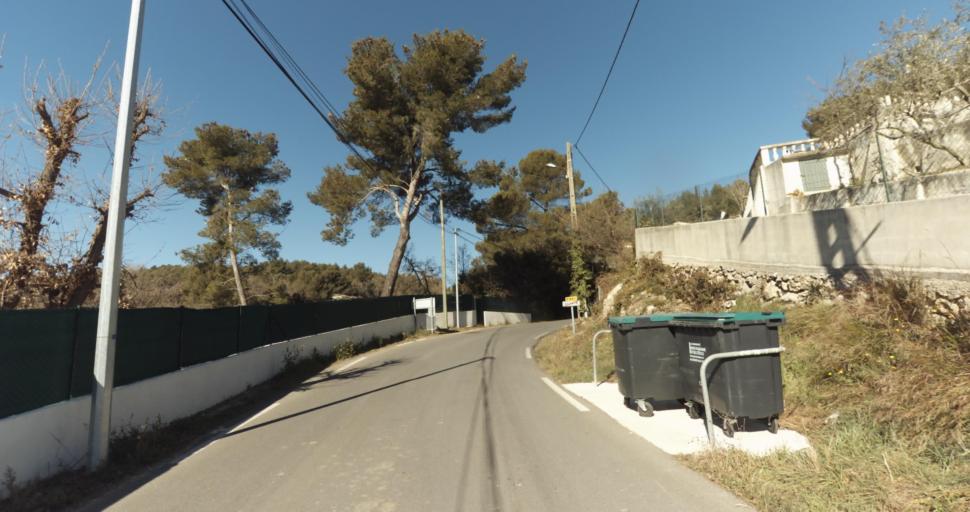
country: FR
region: Provence-Alpes-Cote d'Azur
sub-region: Departement des Bouches-du-Rhone
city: Peypin
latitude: 43.3878
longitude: 5.5778
